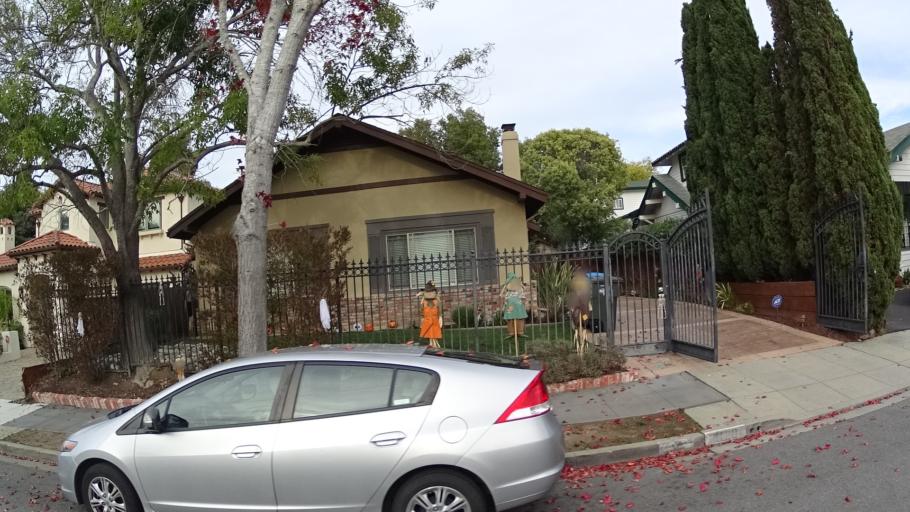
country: US
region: California
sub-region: San Mateo County
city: Burlingame
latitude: 37.5801
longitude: -122.3680
